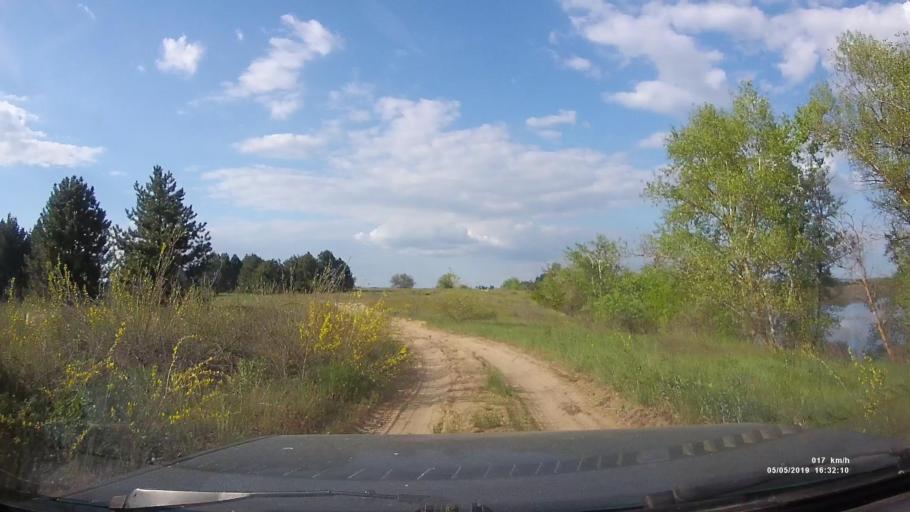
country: RU
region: Rostov
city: Ust'-Donetskiy
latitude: 47.7781
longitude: 41.0141
